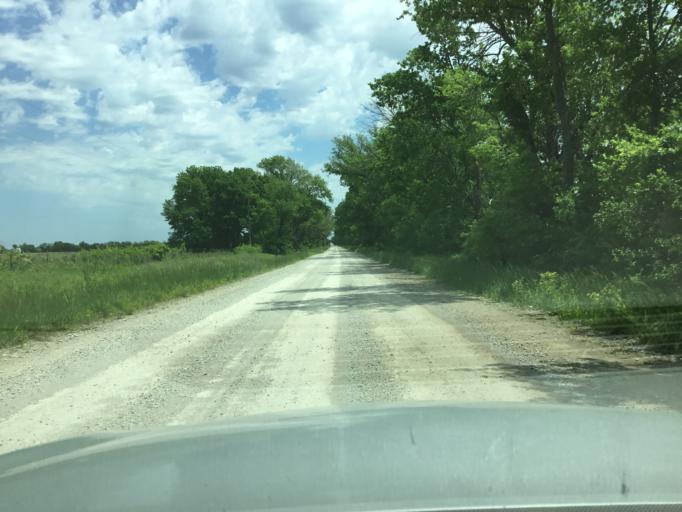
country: US
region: Kansas
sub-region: Montgomery County
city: Independence
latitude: 37.1095
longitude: -95.7752
